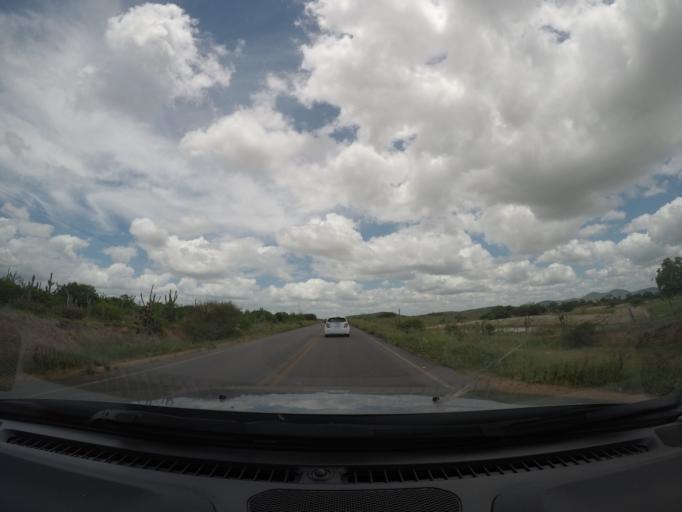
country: BR
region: Bahia
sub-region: Ipira
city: Ipira
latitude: -12.2785
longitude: -39.8571
